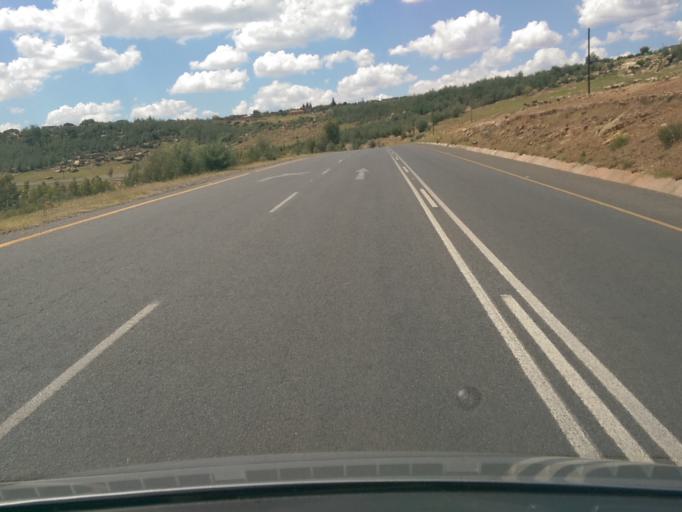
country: LS
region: Maseru
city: Maseru
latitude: -29.3981
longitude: 27.5286
